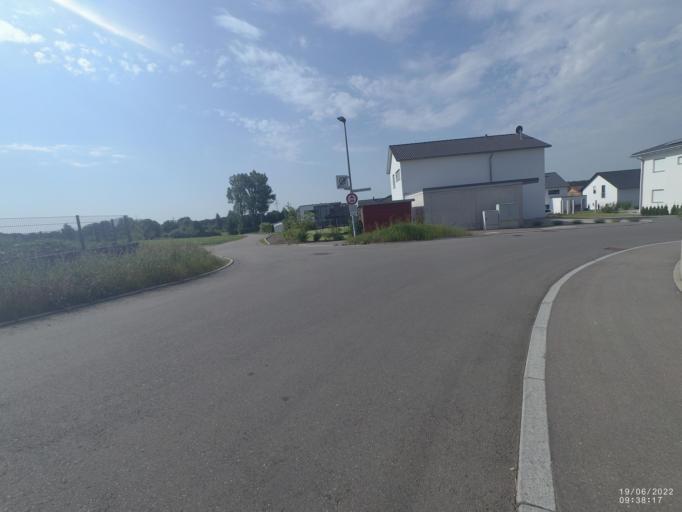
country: DE
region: Baden-Wuerttemberg
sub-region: Regierungsbezirk Stuttgart
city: Gerstetten
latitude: 48.6160
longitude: 10.0188
